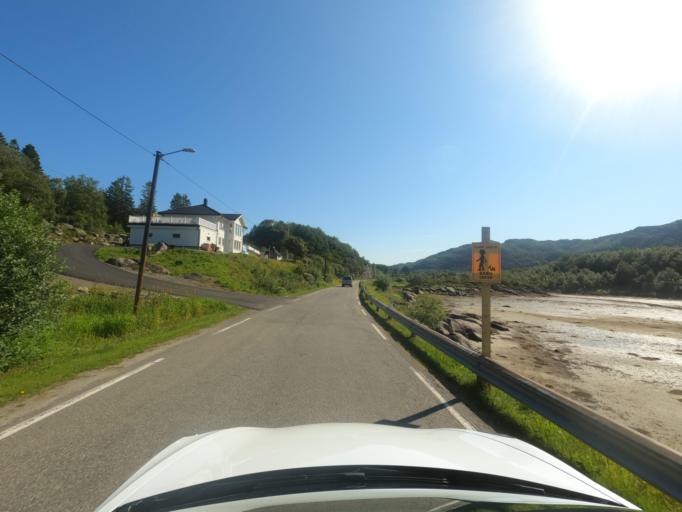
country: NO
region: Nordland
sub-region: Hadsel
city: Stokmarknes
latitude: 68.3046
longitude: 15.0065
